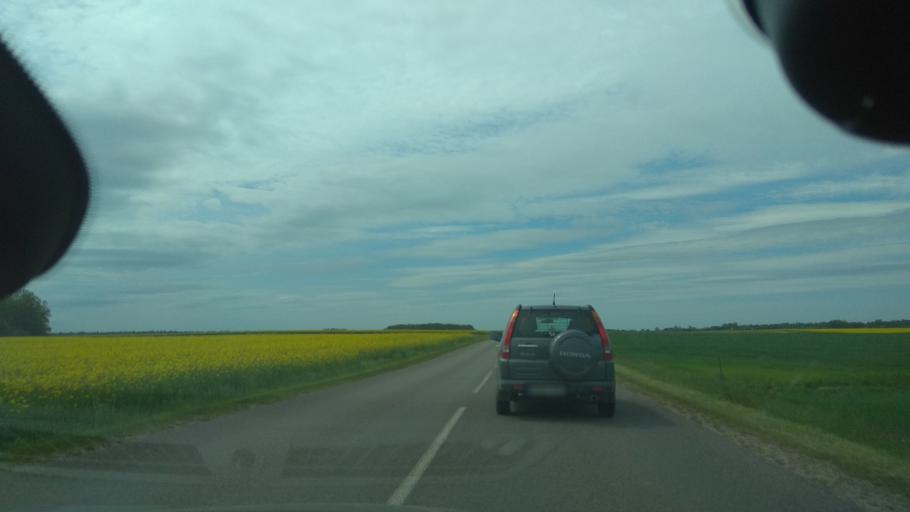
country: LT
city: Sirvintos
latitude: 55.0714
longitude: 24.8627
